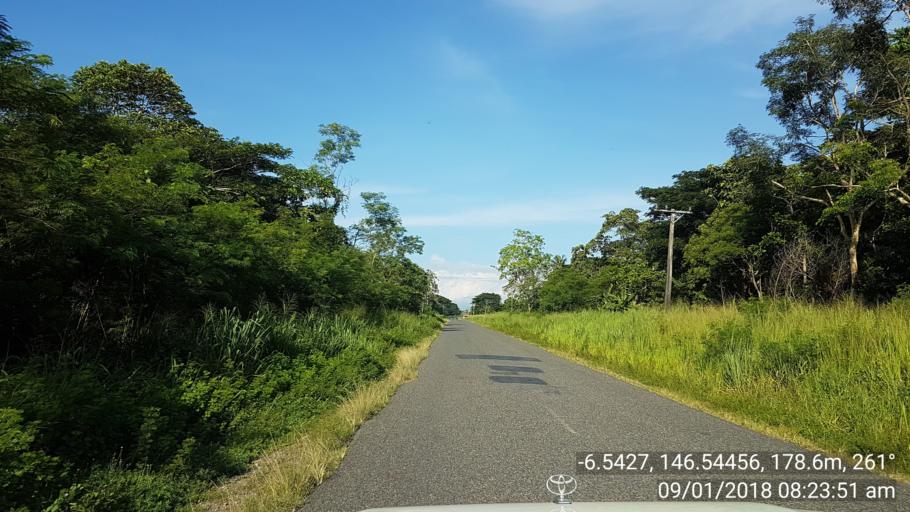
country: PG
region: Morobe
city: Lae
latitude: -6.5426
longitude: 146.5440
